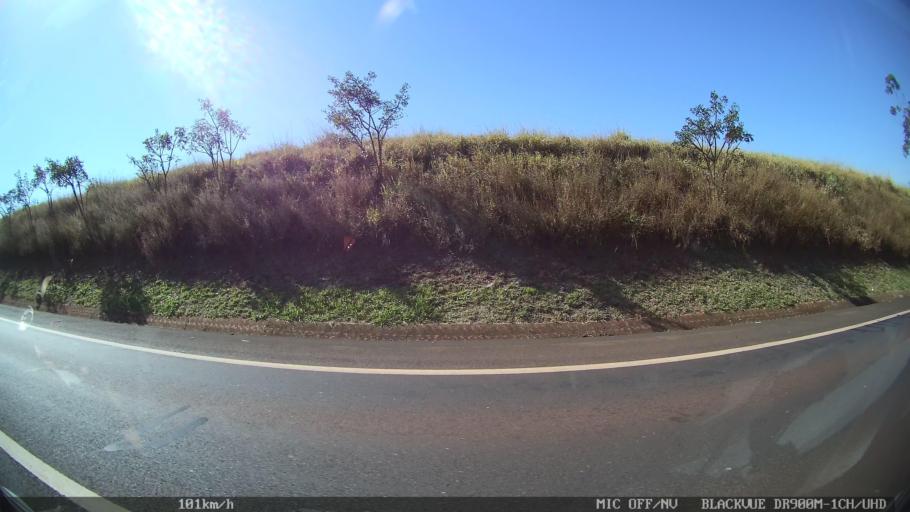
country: BR
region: Sao Paulo
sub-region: Batatais
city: Batatais
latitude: -20.8397
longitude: -47.6015
